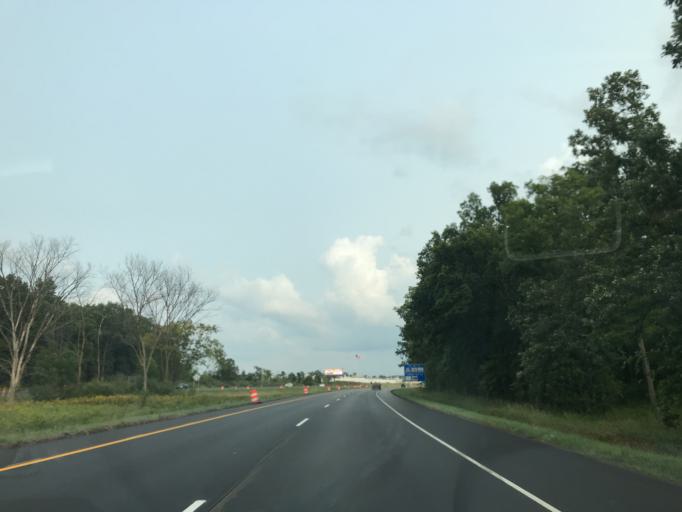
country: US
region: Michigan
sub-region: Livingston County
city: Fowlerville
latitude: 42.6266
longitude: -84.0059
